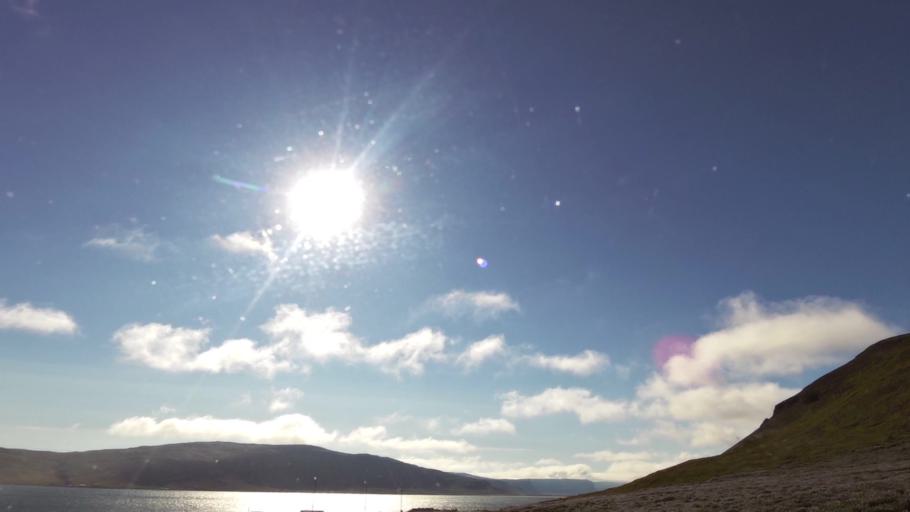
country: IS
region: West
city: Olafsvik
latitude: 65.5433
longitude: -23.8754
